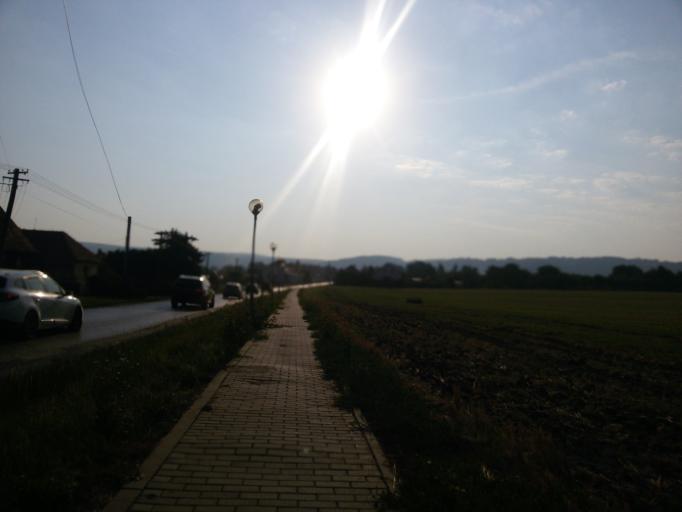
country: CZ
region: South Moravian
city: Drasov
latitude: 49.3314
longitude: 16.4898
